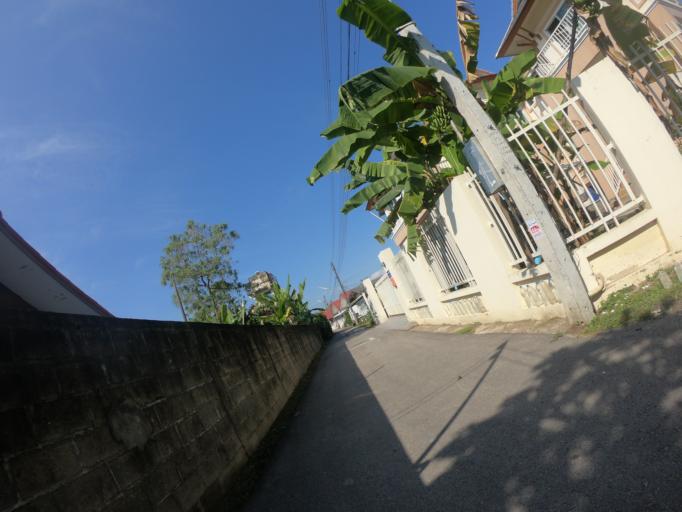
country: TH
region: Chiang Mai
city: Saraphi
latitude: 18.7731
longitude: 99.0433
